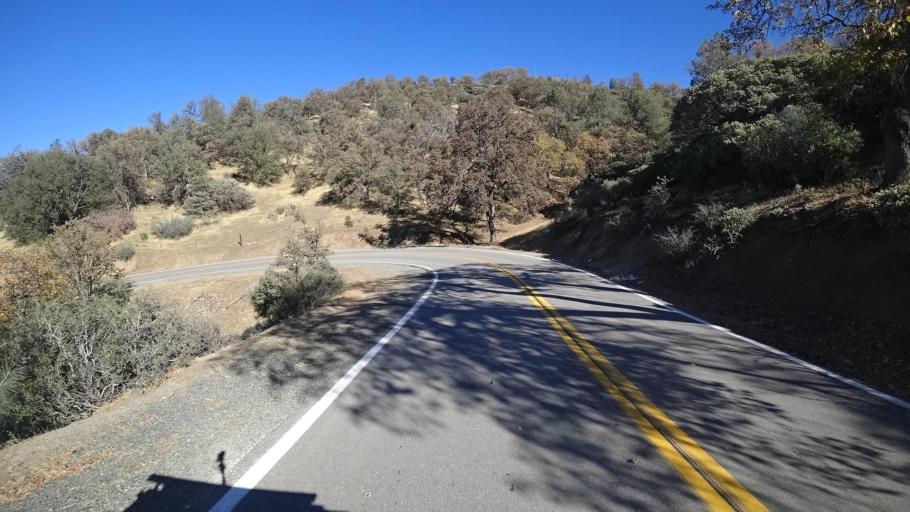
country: US
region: California
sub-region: Kern County
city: Alta Sierra
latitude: 35.7372
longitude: -118.6171
